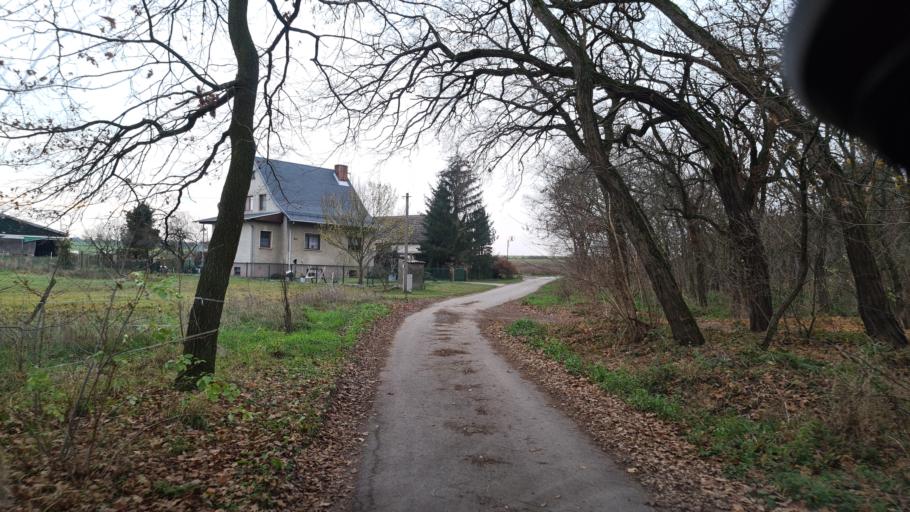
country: DE
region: Brandenburg
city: Schenkendobern
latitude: 51.9595
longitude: 14.6276
